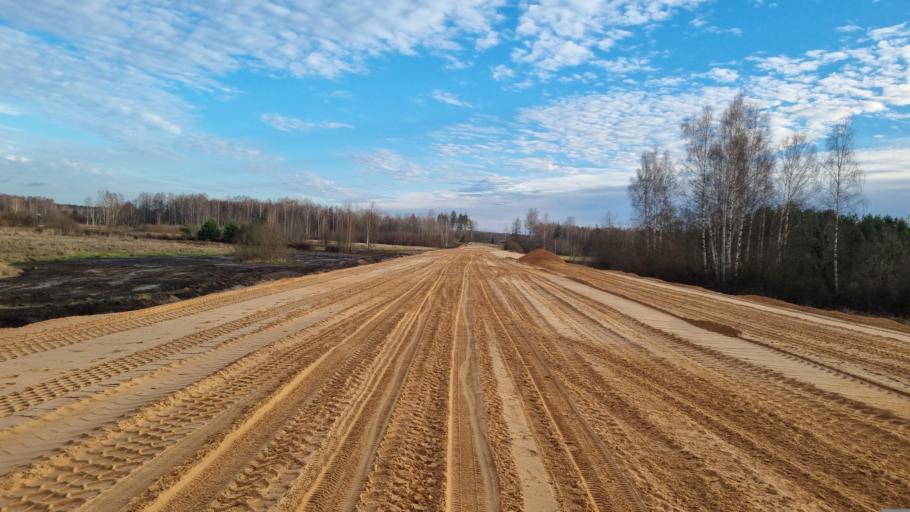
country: LV
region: Kekava
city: Kekava
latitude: 56.7849
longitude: 24.2278
